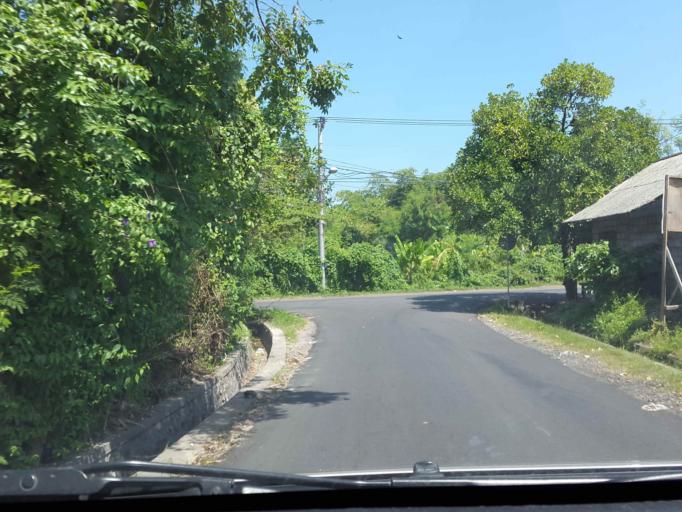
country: ID
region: Bali
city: Semarapura
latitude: -8.5524
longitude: 115.4003
